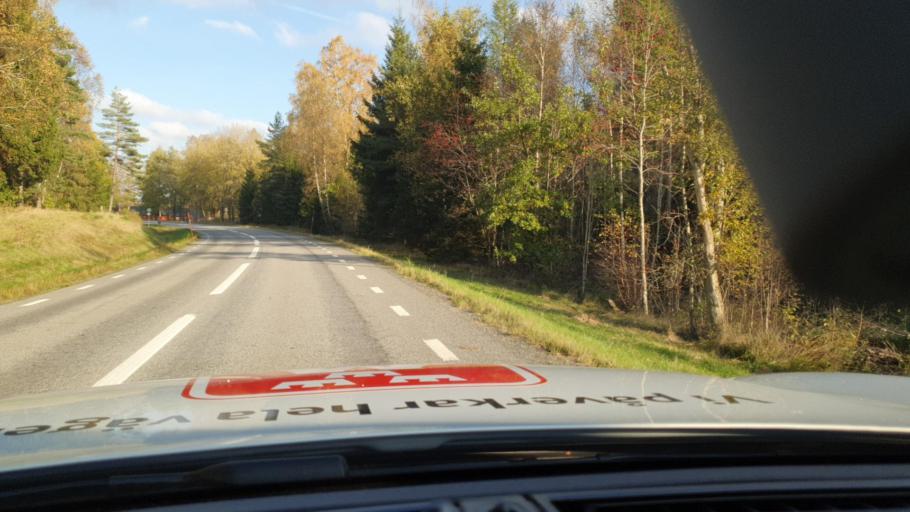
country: SE
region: Kronoberg
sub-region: Ljungby Kommun
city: Ljungby
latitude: 56.8191
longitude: 13.7977
